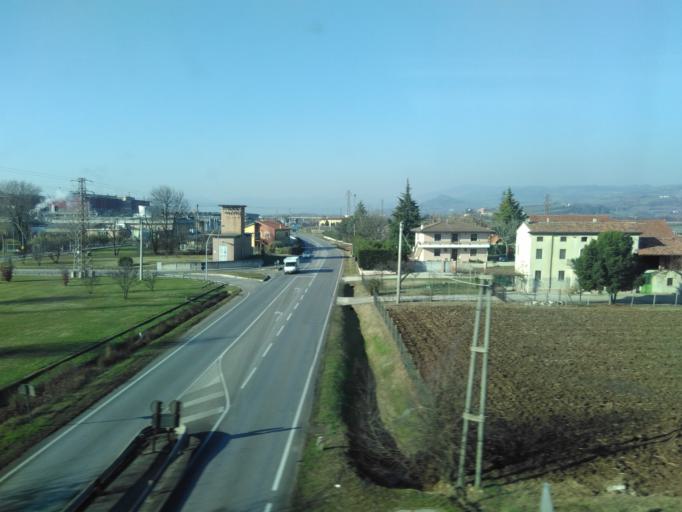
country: IT
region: Veneto
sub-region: Provincia di Vicenza
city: Monticello di Fara
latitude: 45.4329
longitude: 11.3677
